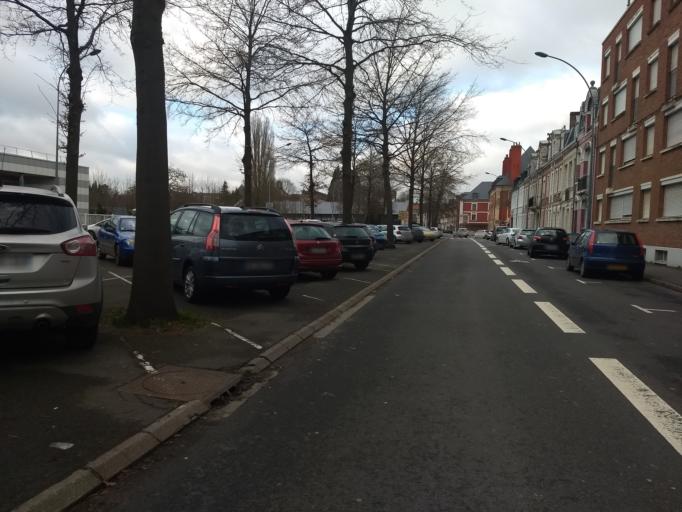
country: FR
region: Nord-Pas-de-Calais
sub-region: Departement du Pas-de-Calais
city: Achicourt
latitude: 50.2881
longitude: 2.7658
